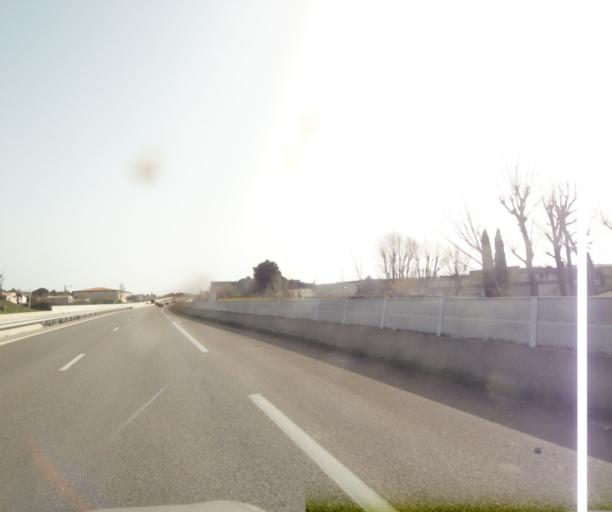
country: FR
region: Provence-Alpes-Cote d'Azur
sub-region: Departement des Bouches-du-Rhone
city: Meyreuil
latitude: 43.4726
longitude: 5.4906
